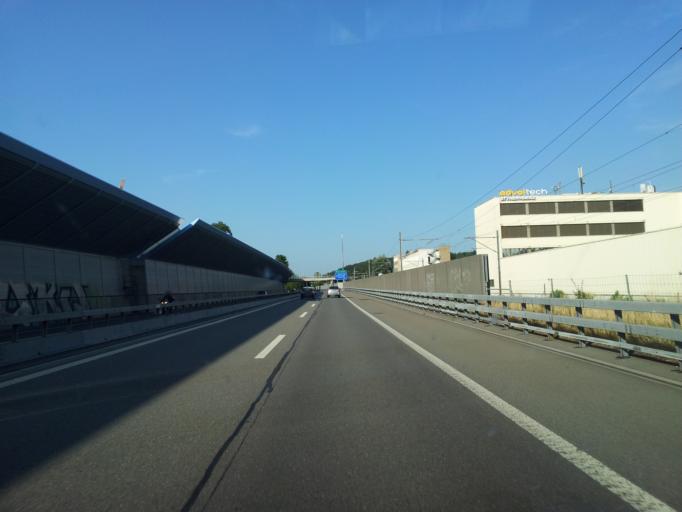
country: CH
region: Bern
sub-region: Bern-Mittelland District
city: Koniz
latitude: 46.9239
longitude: 7.3731
